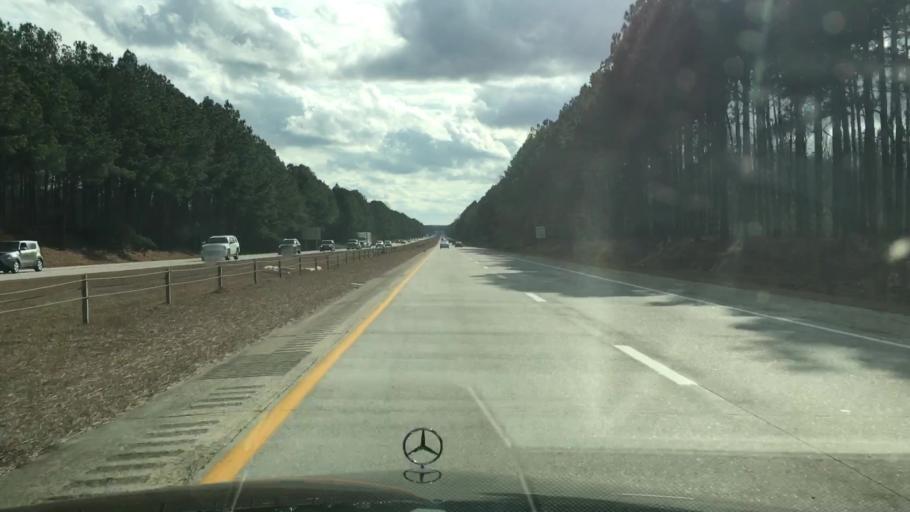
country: US
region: North Carolina
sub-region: Johnston County
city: Benson
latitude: 35.5077
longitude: -78.5554
